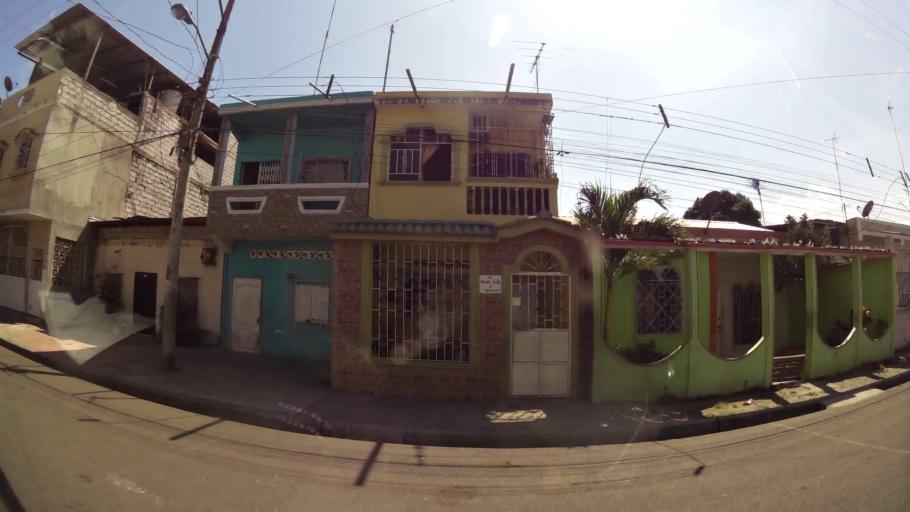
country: EC
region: Guayas
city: Guayaquil
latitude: -2.2215
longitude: -79.9443
